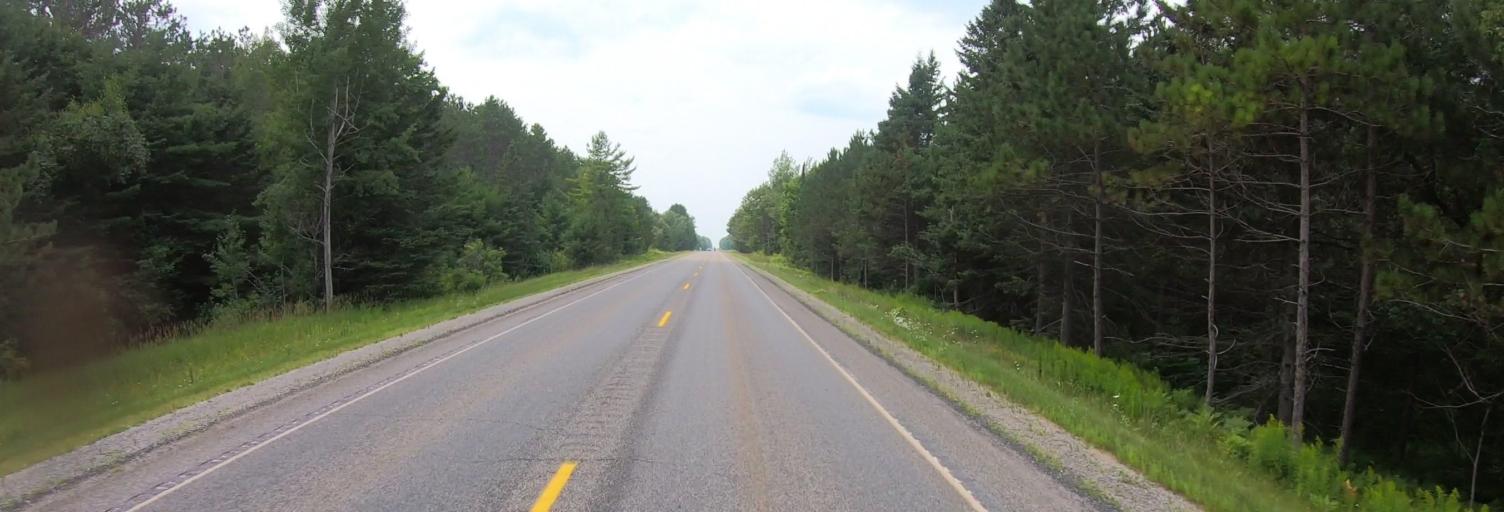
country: US
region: Michigan
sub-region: Alger County
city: Munising
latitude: 46.3329
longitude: -86.7735
